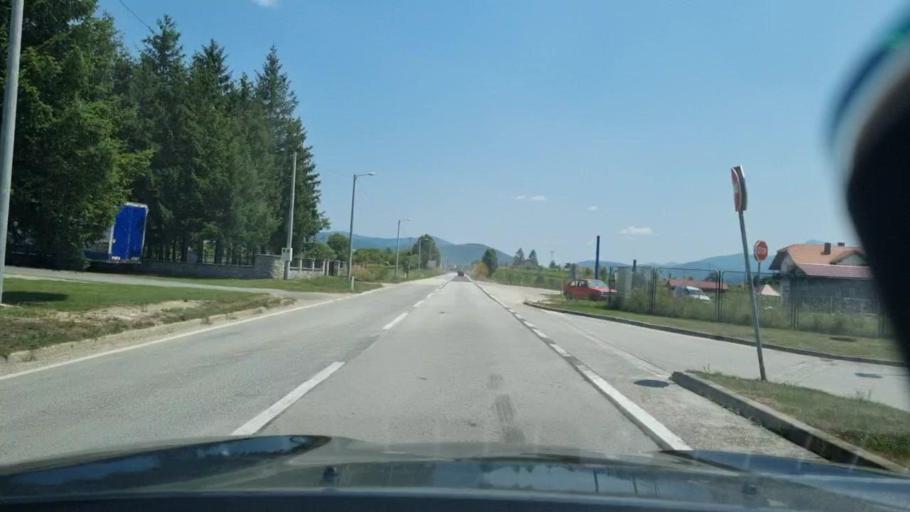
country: BA
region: Federation of Bosnia and Herzegovina
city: Sanica
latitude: 44.5466
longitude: 16.3589
